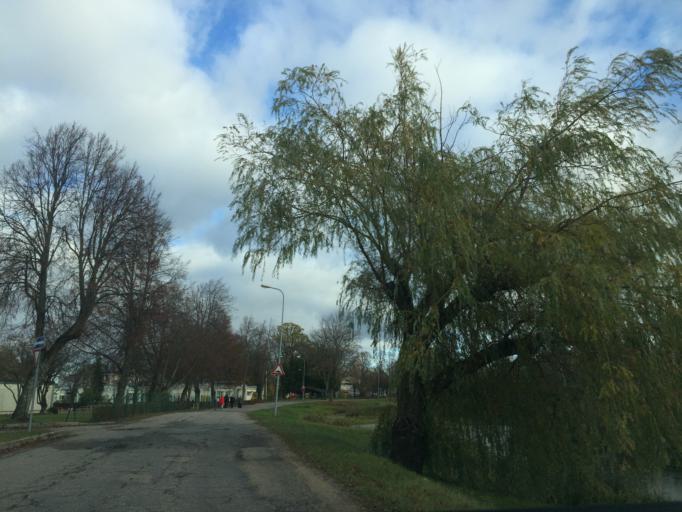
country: LV
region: Carnikava
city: Carnikava
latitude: 57.1284
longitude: 24.2708
